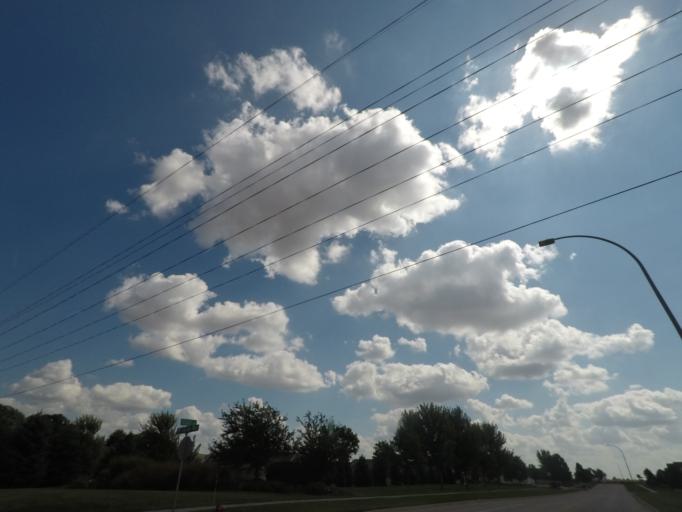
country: US
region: Iowa
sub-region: Story County
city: Nevada
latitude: 42.0228
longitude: -93.4724
